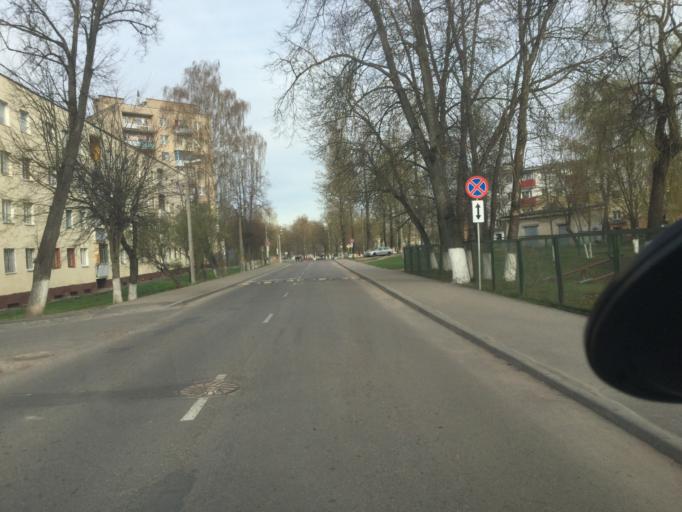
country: BY
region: Vitebsk
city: Vitebsk
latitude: 55.1729
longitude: 30.1412
